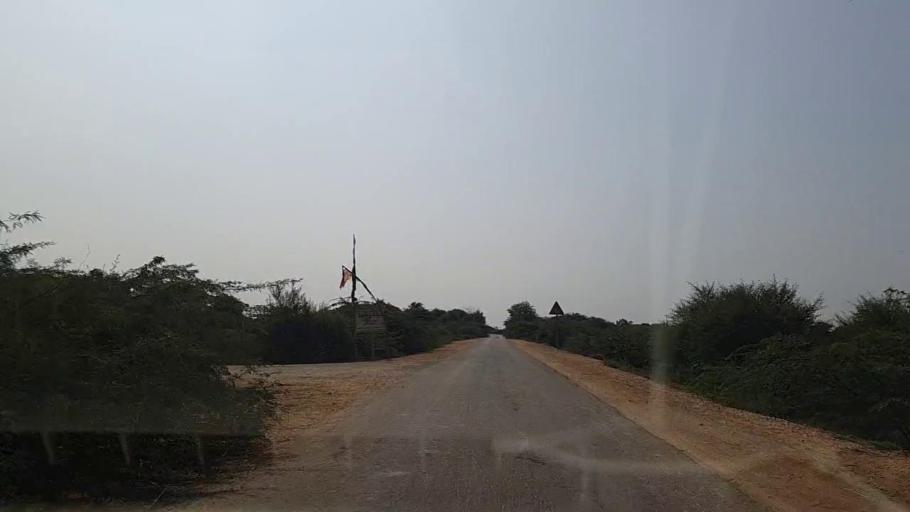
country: PK
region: Sindh
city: Chuhar Jamali
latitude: 24.2687
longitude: 67.9113
